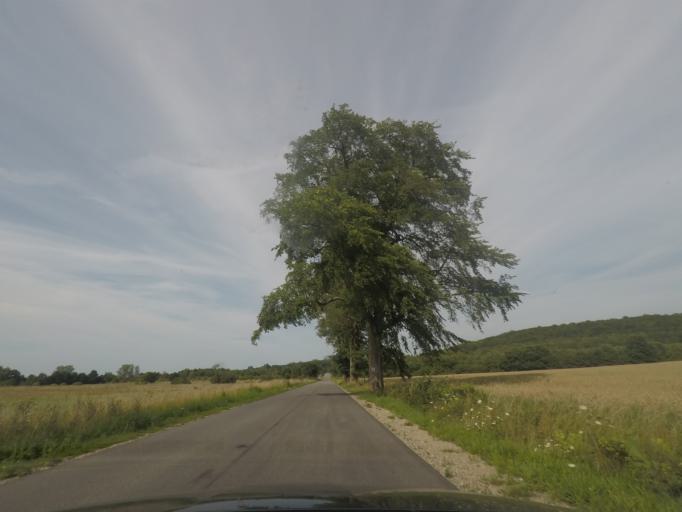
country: PL
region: Pomeranian Voivodeship
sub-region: Powiat slupski
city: Smoldzino
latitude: 54.6126
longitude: 17.1339
